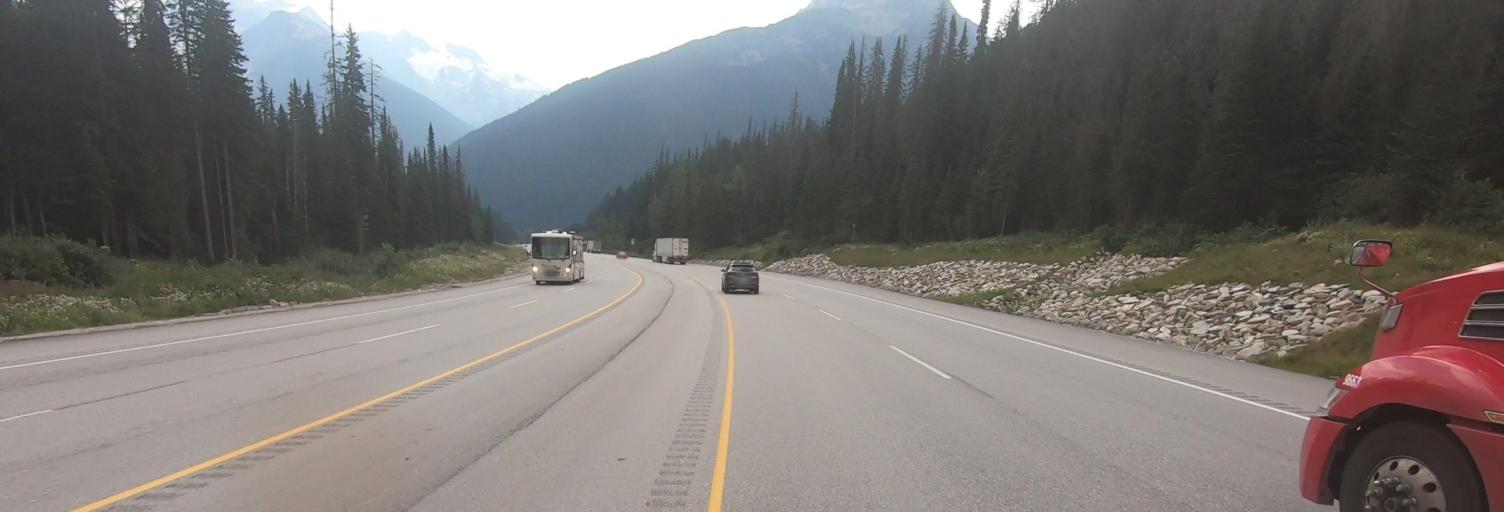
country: CA
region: British Columbia
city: Golden
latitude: 51.2828
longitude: -117.5136
